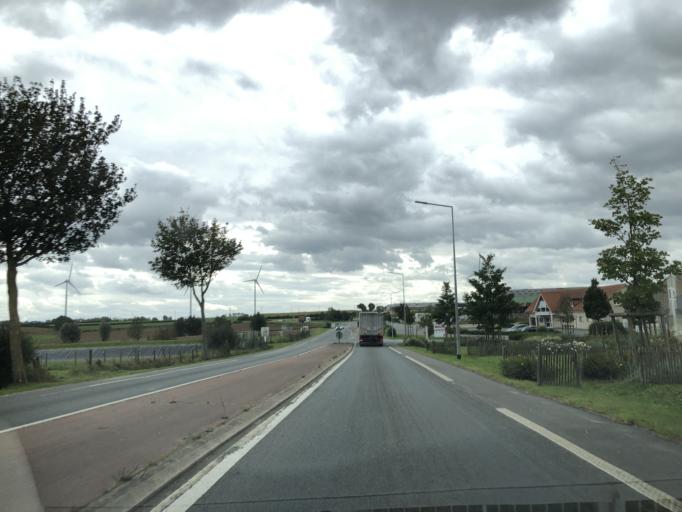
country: FR
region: Nord-Pas-de-Calais
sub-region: Departement du Pas-de-Calais
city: Fruges
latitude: 50.5038
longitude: 2.1307
